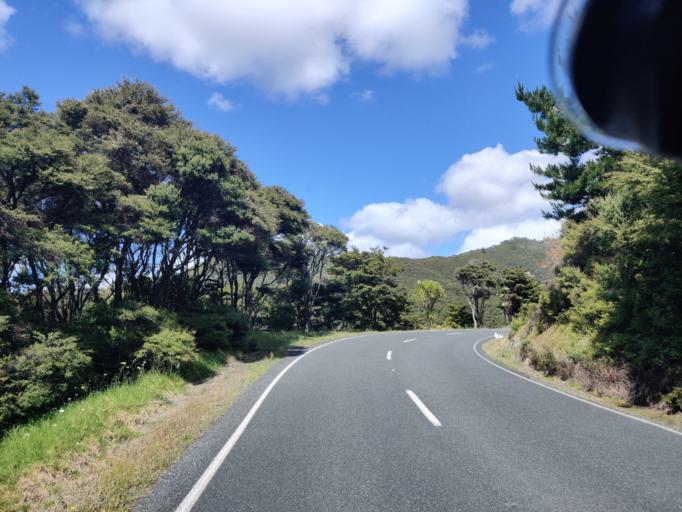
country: NZ
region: Northland
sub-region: Far North District
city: Paihia
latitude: -35.2690
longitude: 174.2747
